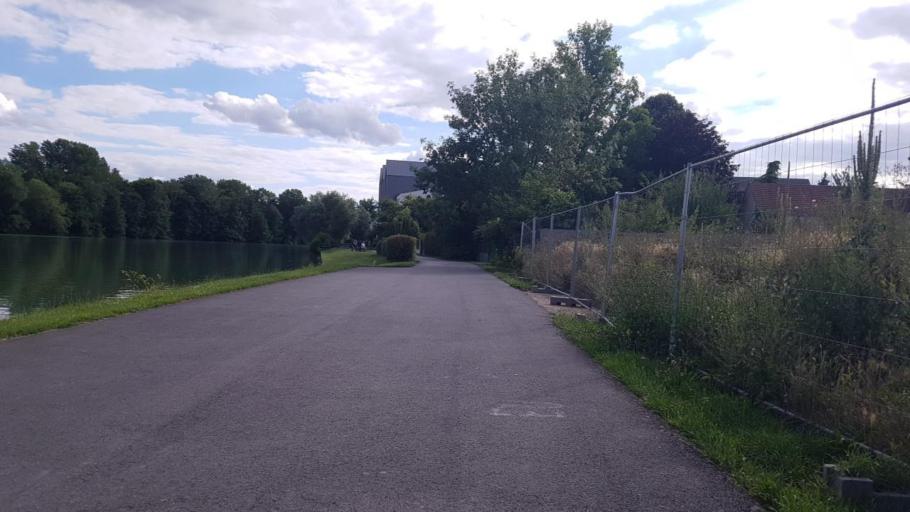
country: FR
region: Picardie
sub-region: Departement de l'Aisne
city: Chateau-Thierry
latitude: 49.0421
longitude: 3.3924
